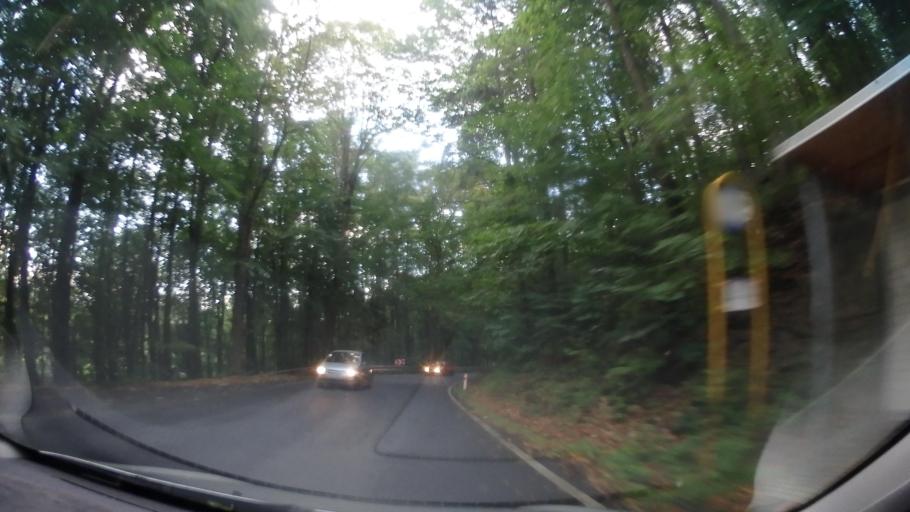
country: CZ
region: Olomoucky
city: Zabreh
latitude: 49.8874
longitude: 16.8163
